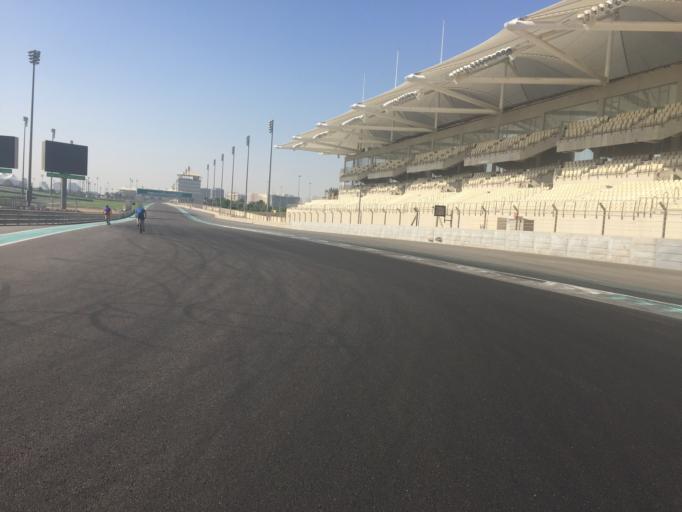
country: AE
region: Abu Dhabi
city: Abu Dhabi
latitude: 24.4790
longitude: 54.6054
